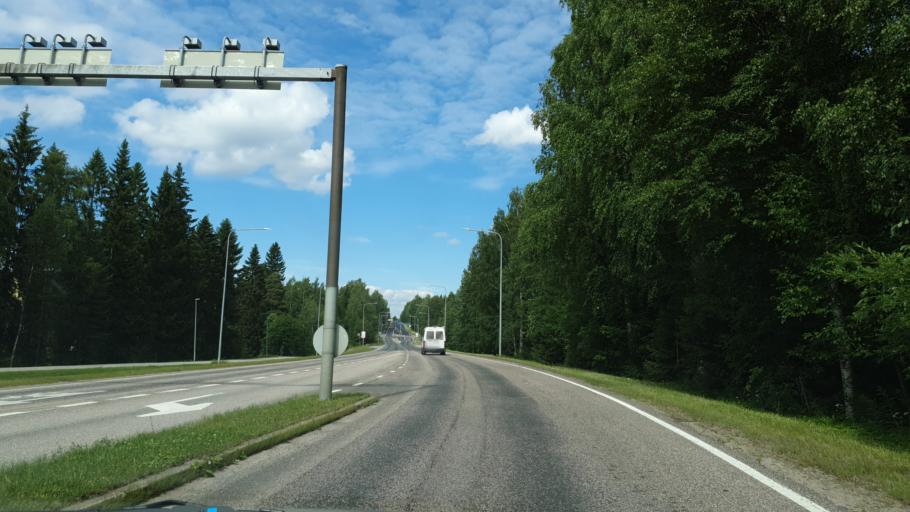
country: FI
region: Kainuu
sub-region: Kajaani
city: Kajaani
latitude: 64.2280
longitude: 27.7434
